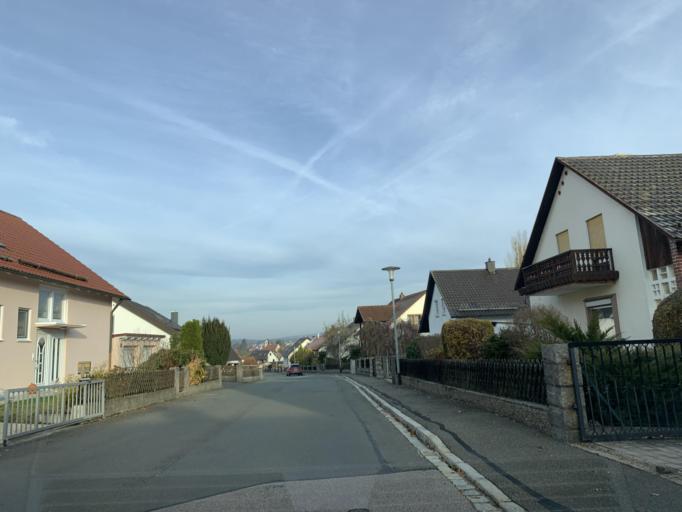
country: DE
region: Bavaria
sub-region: Upper Palatinate
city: Neunburg vorm Wald
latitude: 49.3444
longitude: 12.3944
